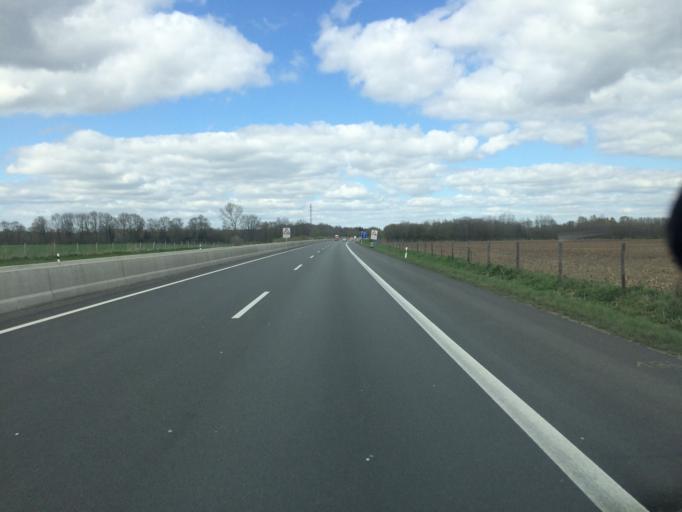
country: DE
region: North Rhine-Westphalia
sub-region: Regierungsbezirk Munster
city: Gescher
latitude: 51.9965
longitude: 7.0497
